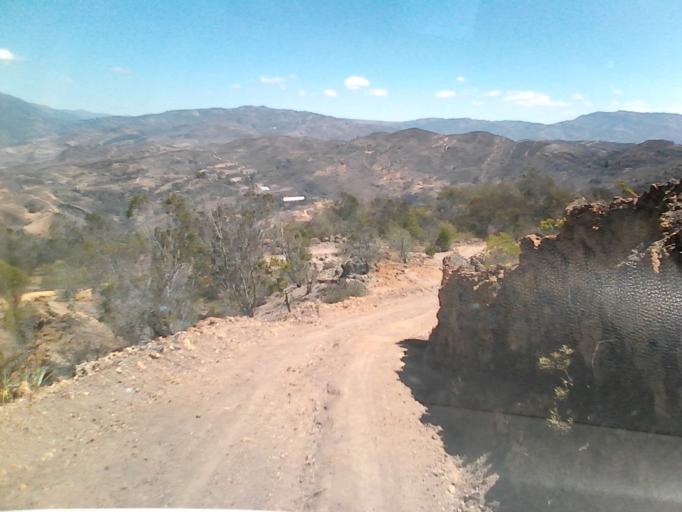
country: CO
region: Boyaca
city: Sachica
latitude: 5.5355
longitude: -73.5420
